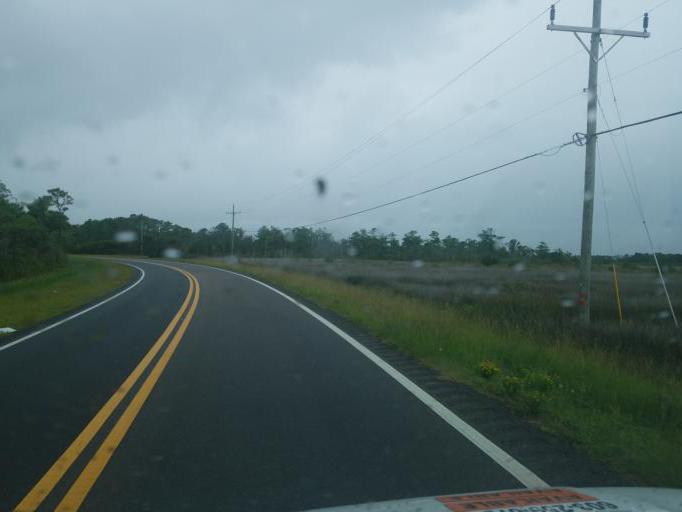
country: US
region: North Carolina
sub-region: Dare County
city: Manteo
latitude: 35.8772
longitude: -75.6546
